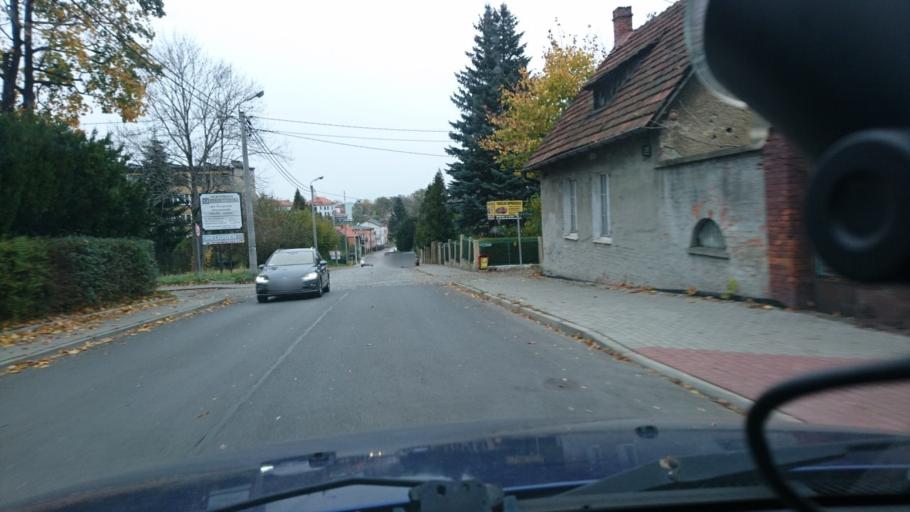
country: PL
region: Silesian Voivodeship
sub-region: Bielsko-Biala
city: Bielsko-Biala
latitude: 49.8302
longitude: 19.0383
